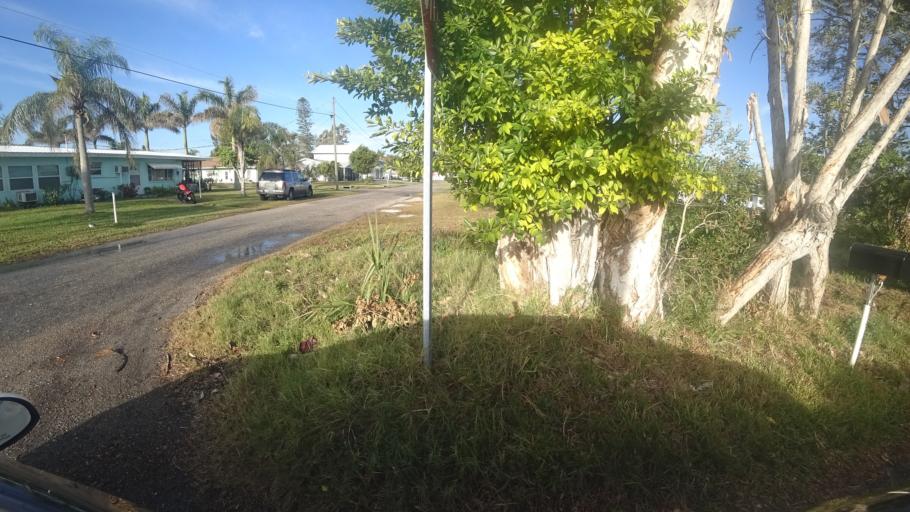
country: US
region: Florida
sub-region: Manatee County
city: Cortez
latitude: 27.4727
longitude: -82.6758
